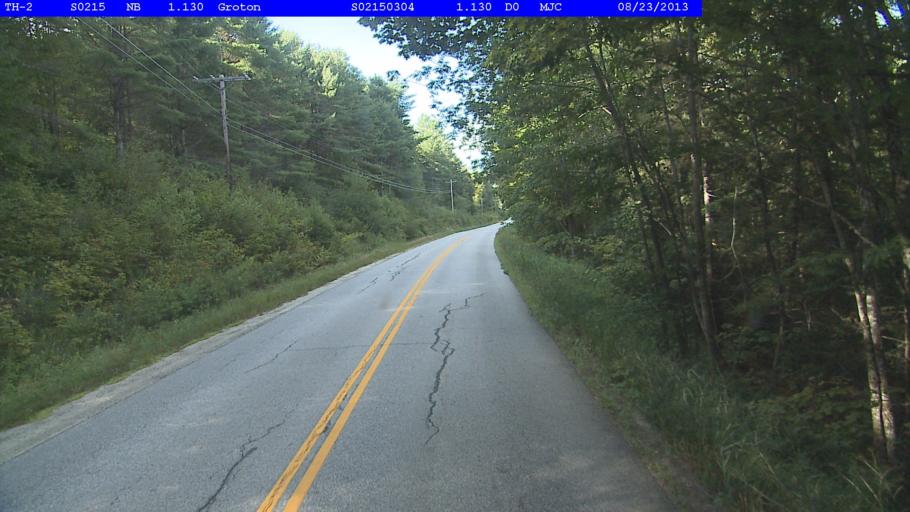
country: US
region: New Hampshire
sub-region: Grafton County
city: Woodsville
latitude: 44.2250
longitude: -72.1907
